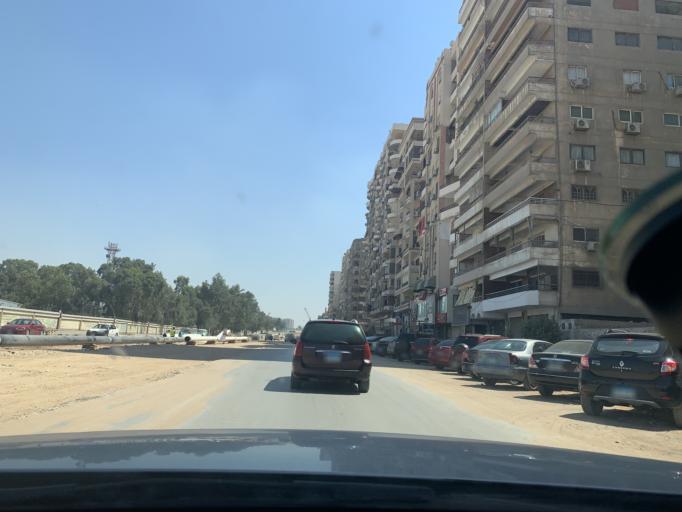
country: EG
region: Muhafazat al Qahirah
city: Cairo
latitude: 30.0519
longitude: 31.3568
